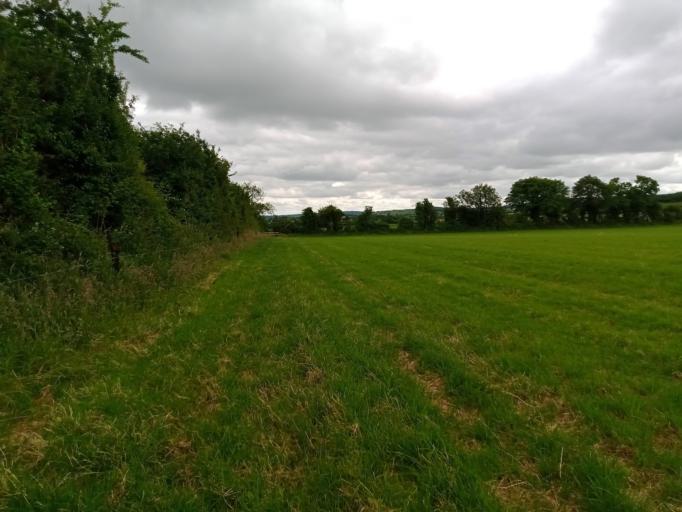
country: IE
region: Leinster
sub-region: Laois
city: Rathdowney
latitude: 52.7837
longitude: -7.4708
